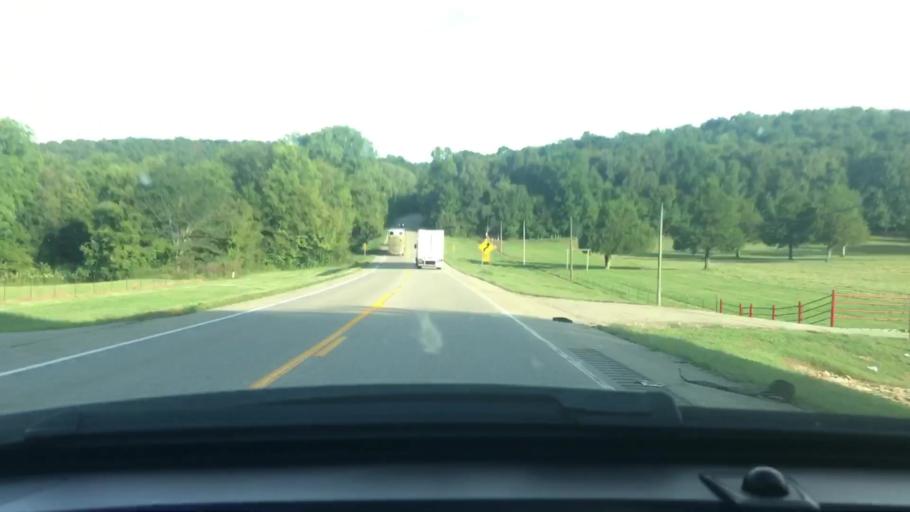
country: US
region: Arkansas
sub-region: Randolph County
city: Pocahontas
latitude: 36.2182
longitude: -91.2195
